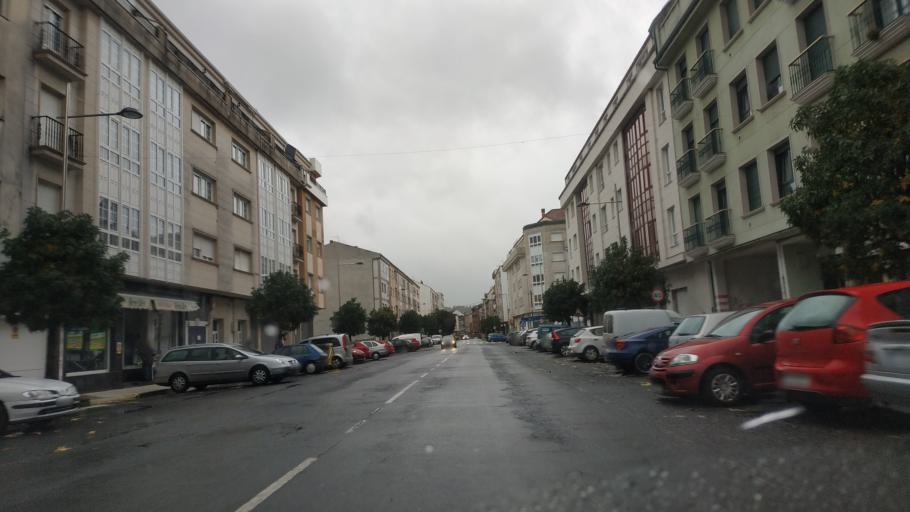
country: ES
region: Galicia
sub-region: Provincia da Coruna
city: Negreira
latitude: 42.9140
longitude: -8.7358
